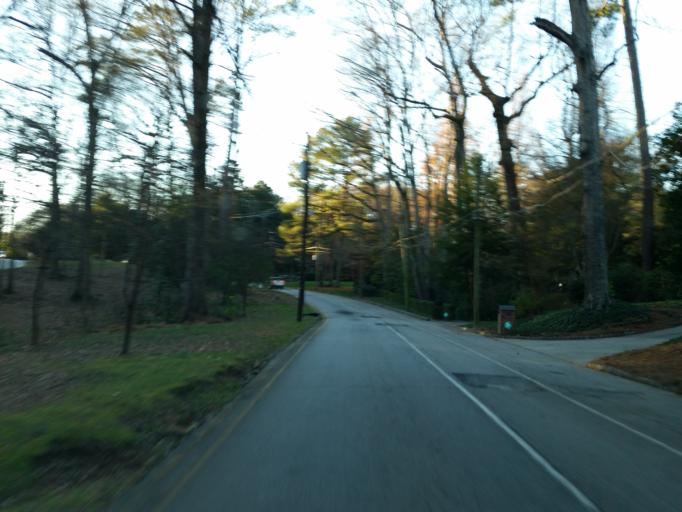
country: US
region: Georgia
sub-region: DeKalb County
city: Druid Hills
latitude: 33.8220
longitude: -84.3944
